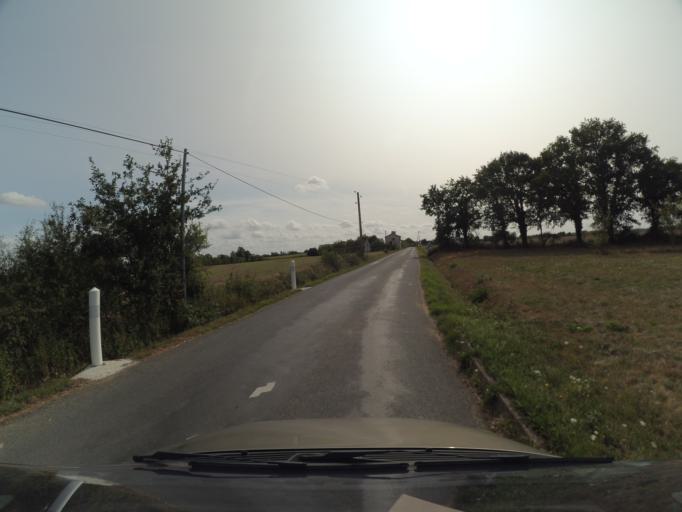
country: FR
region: Pays de la Loire
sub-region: Departement de la Loire-Atlantique
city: Boussay
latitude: 47.0222
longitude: -1.1567
